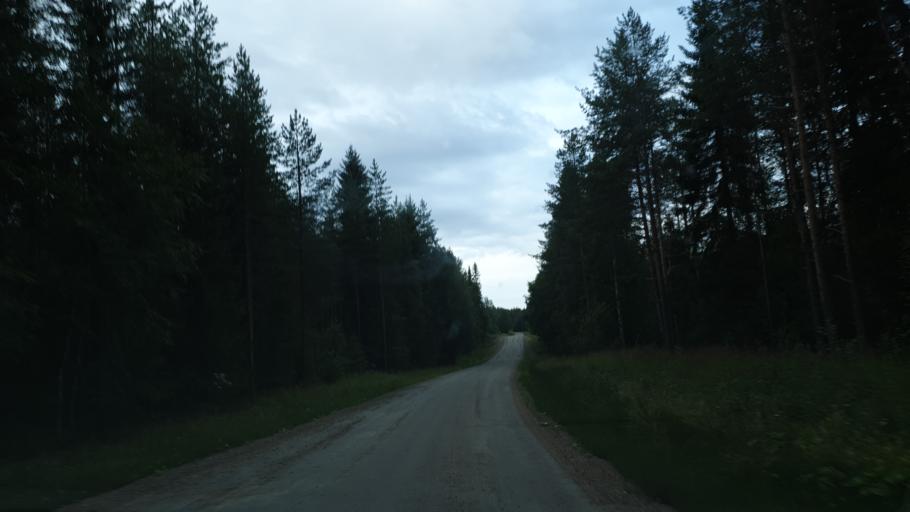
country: FI
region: Kainuu
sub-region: Kehys-Kainuu
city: Kuhmo
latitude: 64.2034
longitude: 29.3731
